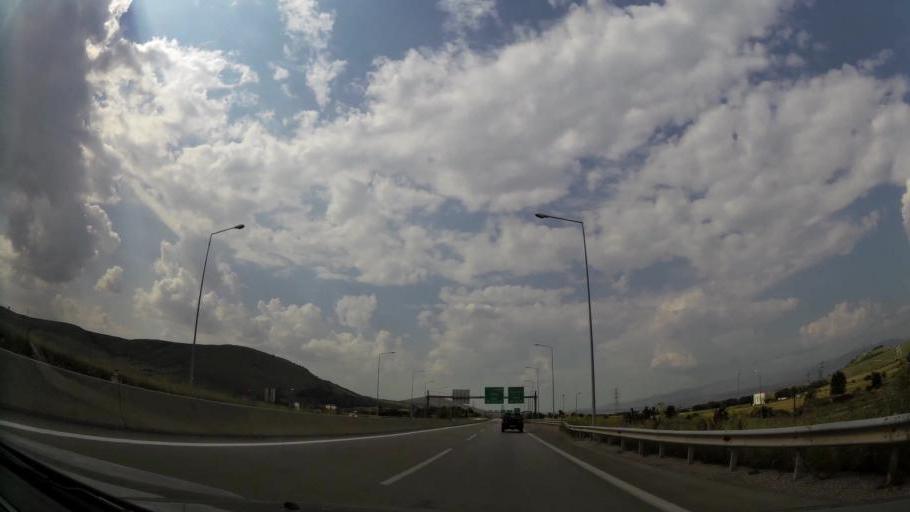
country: GR
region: West Macedonia
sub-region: Nomos Kozanis
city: Koila
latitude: 40.3433
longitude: 21.8066
